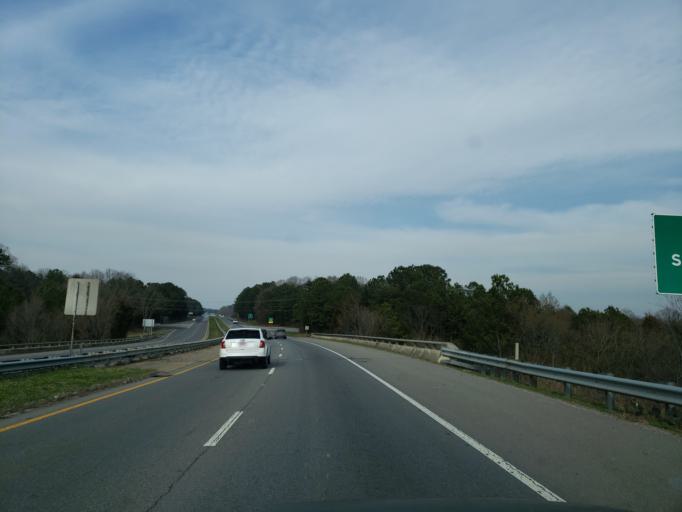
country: US
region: Tennessee
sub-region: Bradley County
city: South Cleveland
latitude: 35.1329
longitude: -84.8604
